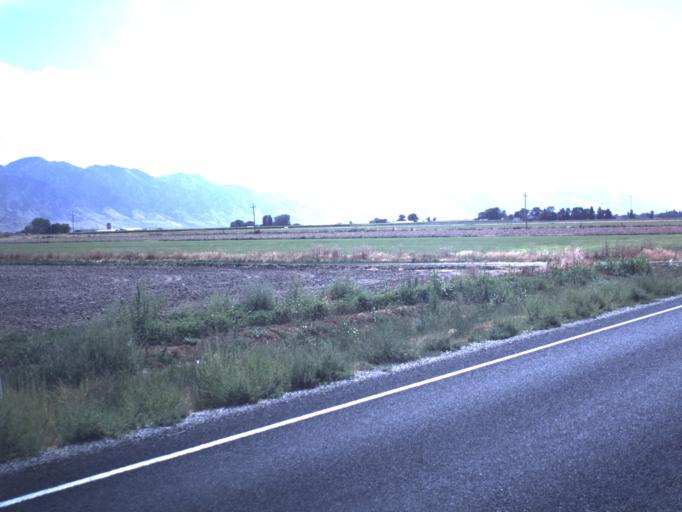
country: US
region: Utah
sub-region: Box Elder County
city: Elwood
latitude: 41.6572
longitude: -112.1405
